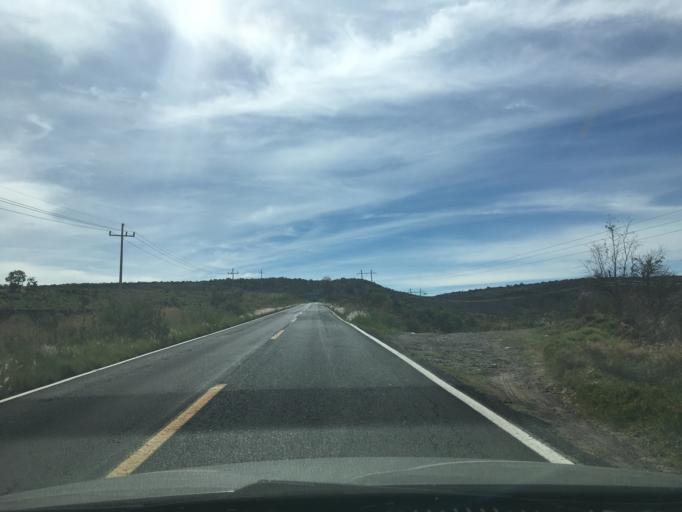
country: MX
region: Guanajuato
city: Coroneo
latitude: 20.1899
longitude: -100.3501
